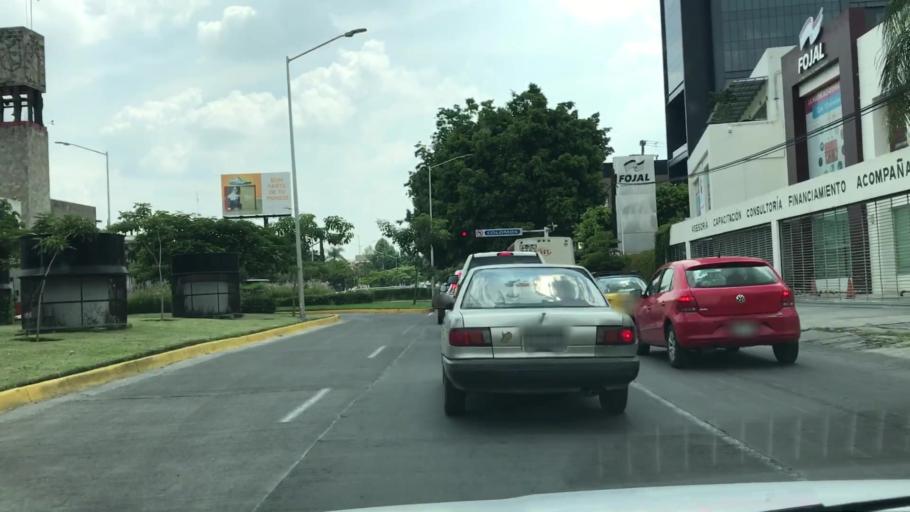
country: MX
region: Jalisco
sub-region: Zapopan
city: Zapopan
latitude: 20.6950
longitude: -103.3739
